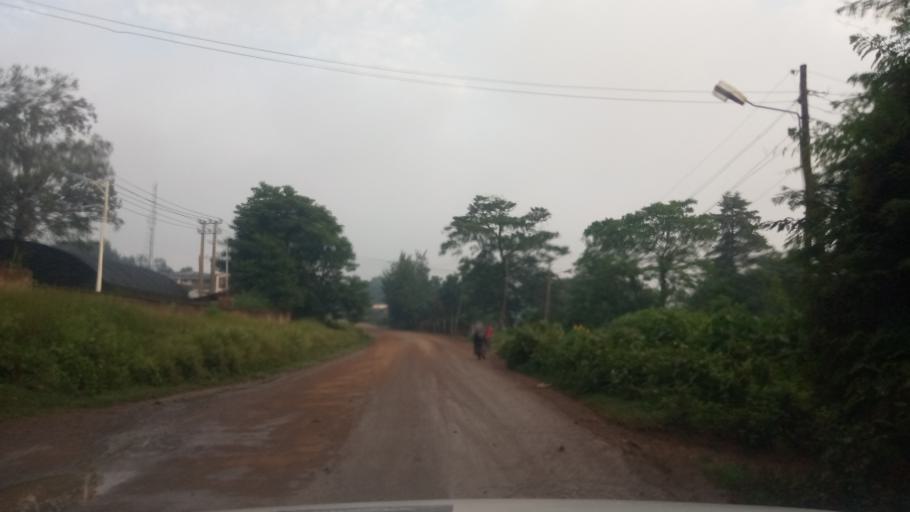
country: ET
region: Oromiya
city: Jima
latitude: 7.6866
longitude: 36.8311
